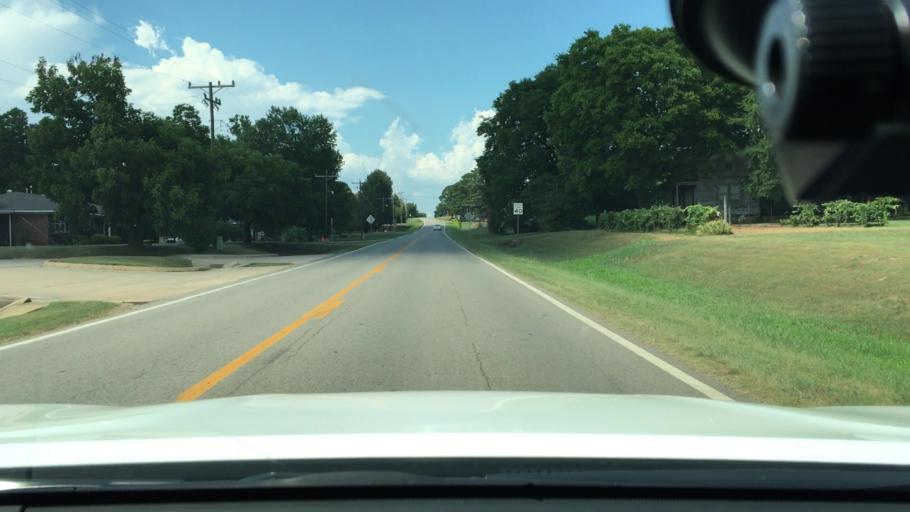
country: US
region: Arkansas
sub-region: Logan County
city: Paris
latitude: 35.2944
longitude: -93.6368
